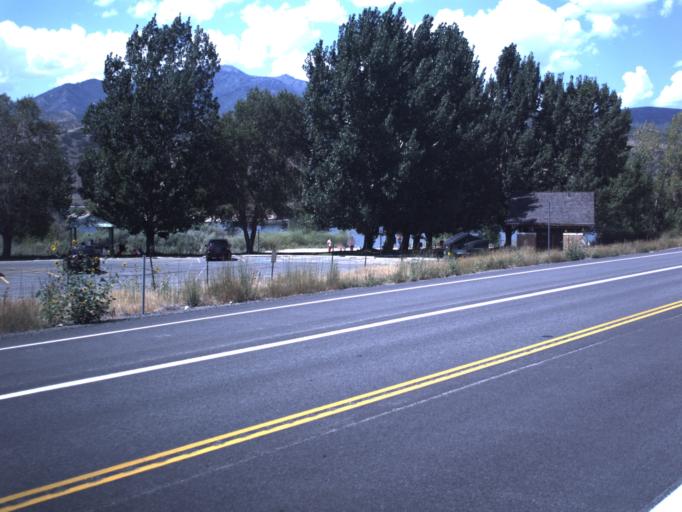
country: US
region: Utah
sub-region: Wasatch County
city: Midway
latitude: 40.4469
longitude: -111.4772
